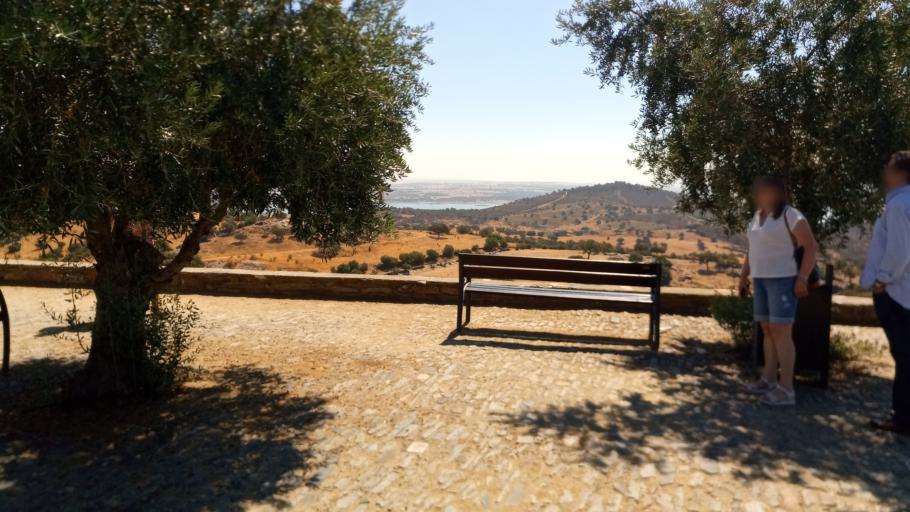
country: PT
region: Evora
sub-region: Mourao
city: Mourao
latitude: 38.4419
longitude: -7.3791
